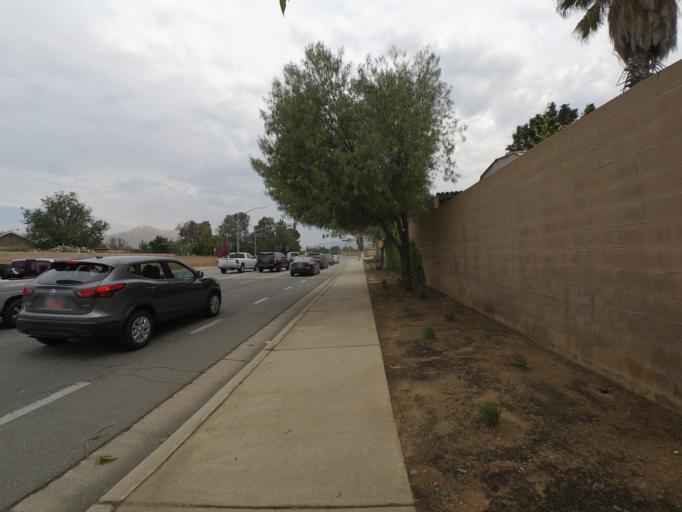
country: US
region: California
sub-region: Riverside County
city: Moreno Valley
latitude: 33.9311
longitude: -117.2524
